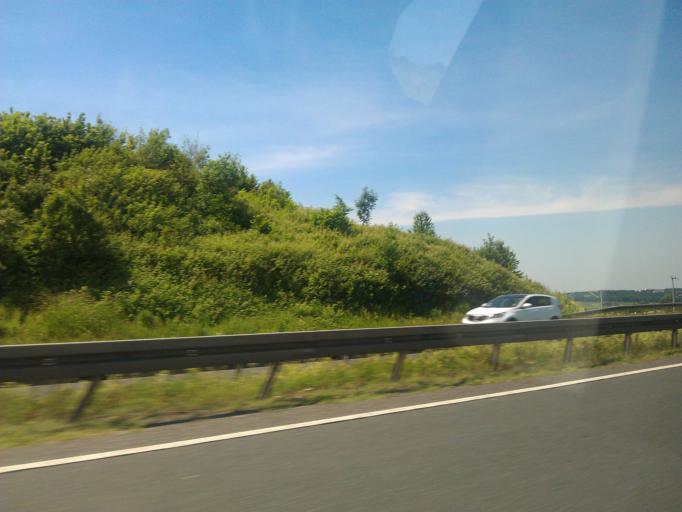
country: DE
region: North Rhine-Westphalia
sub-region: Regierungsbezirk Koln
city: Konigswinter
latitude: 50.7183
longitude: 7.2407
